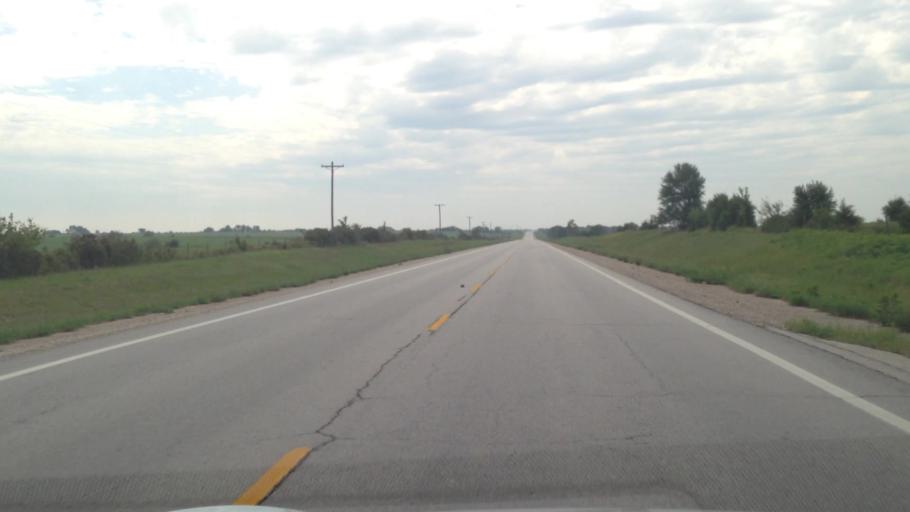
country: US
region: Kansas
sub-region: Anderson County
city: Garnett
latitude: 38.1302
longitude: -95.2425
